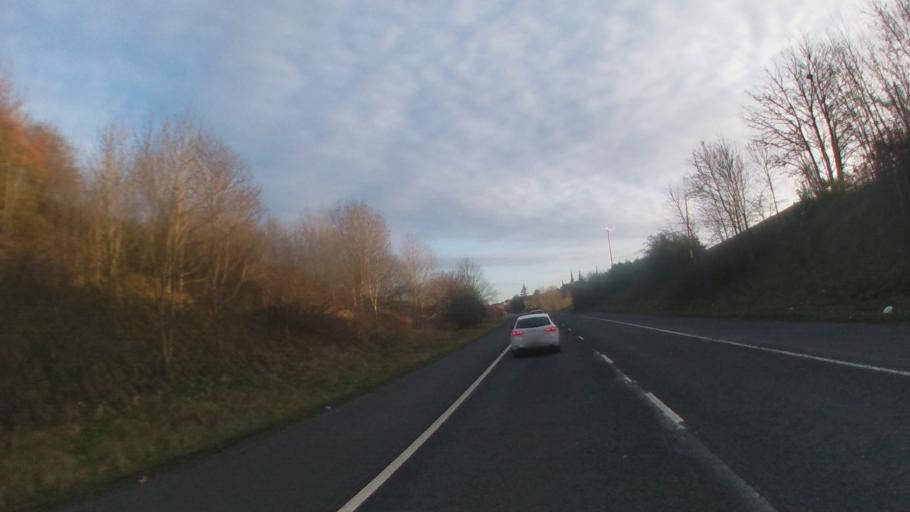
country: GB
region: Northern Ireland
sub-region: Dungannon District
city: Dungannon
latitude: 54.4855
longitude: -6.7421
